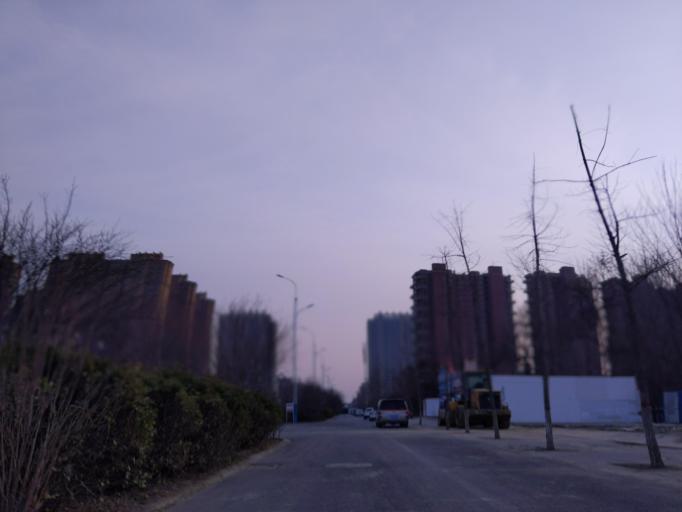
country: CN
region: Henan Sheng
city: Zhongyuanlu
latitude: 35.7848
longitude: 115.1273
